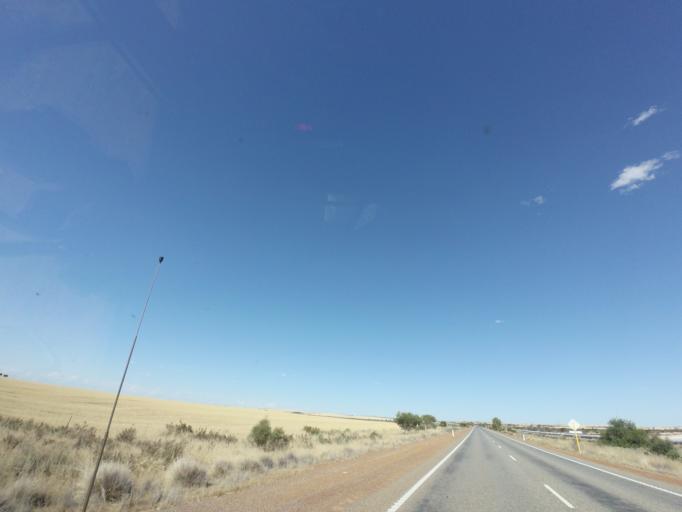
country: AU
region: Western Australia
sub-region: Merredin
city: Merredin
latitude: -31.5808
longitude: 117.9670
